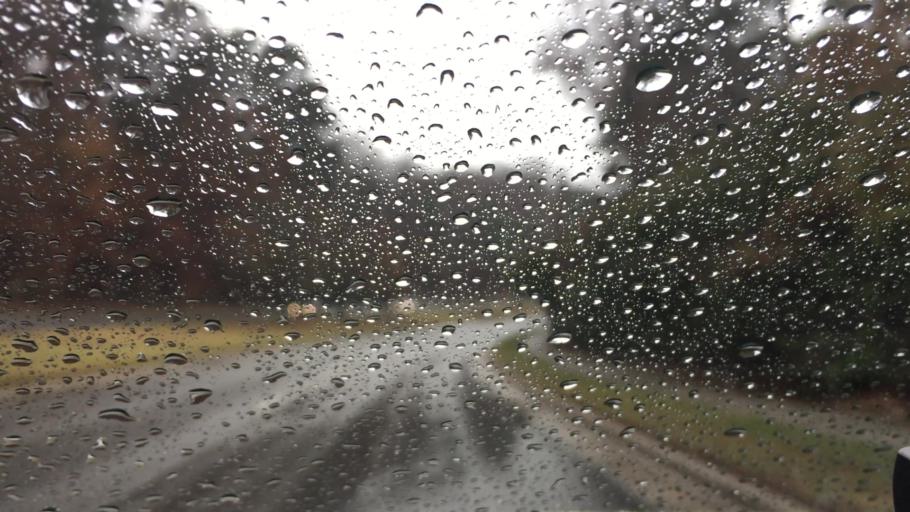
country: US
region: North Carolina
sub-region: Wake County
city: Cary
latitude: 35.7568
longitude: -78.7934
